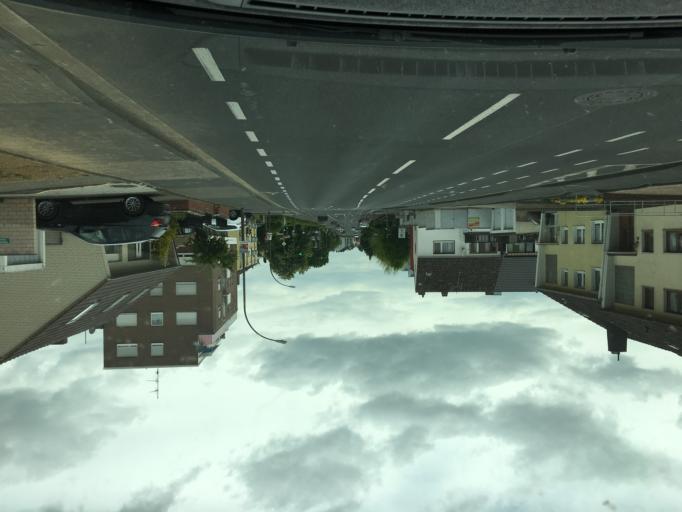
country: DE
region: North Rhine-Westphalia
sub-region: Regierungsbezirk Koln
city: Euskirchen
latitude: 50.6649
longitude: 6.7986
